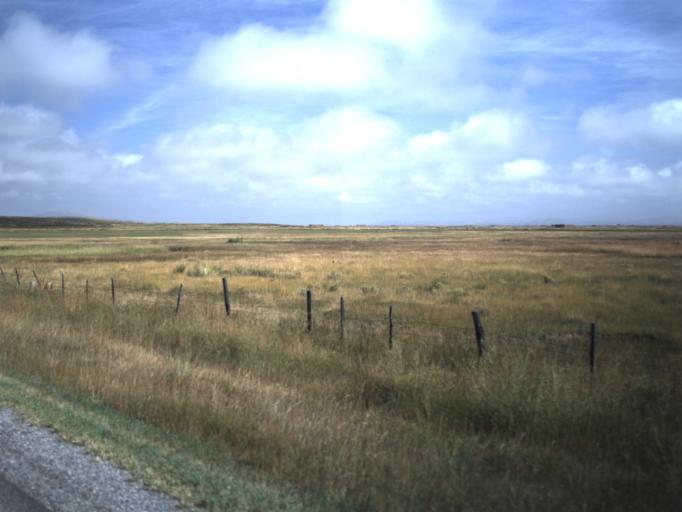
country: US
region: Utah
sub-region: Rich County
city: Randolph
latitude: 41.7207
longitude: -111.1592
